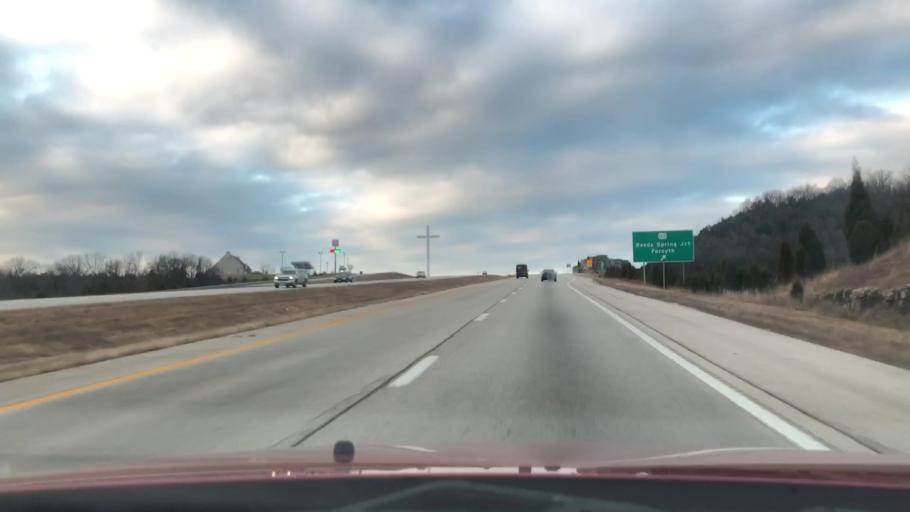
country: US
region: Missouri
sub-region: Taney County
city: Merriam Woods
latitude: 36.7433
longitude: -93.2221
